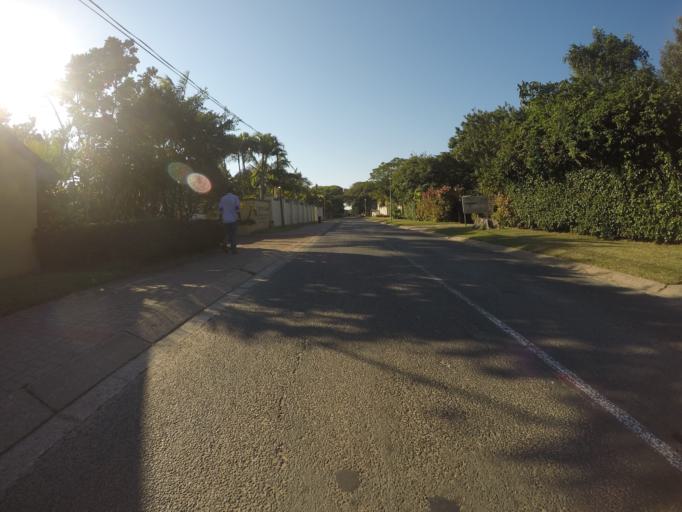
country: ZA
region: KwaZulu-Natal
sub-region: uThungulu District Municipality
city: Richards Bay
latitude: -28.7944
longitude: 32.0966
